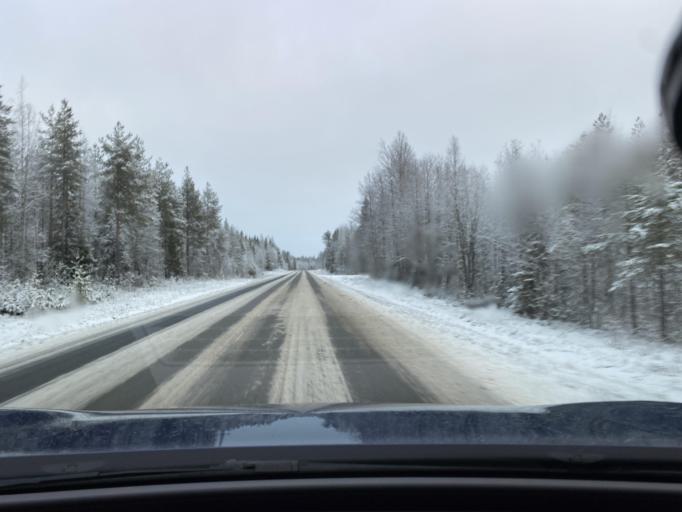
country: FI
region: Lapland
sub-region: Rovaniemi
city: Ranua
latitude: 66.0061
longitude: 26.2705
